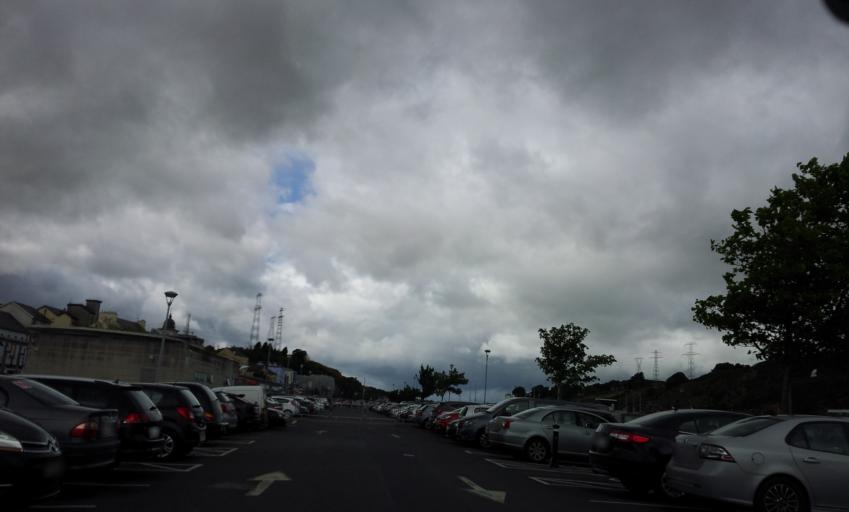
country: IE
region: Munster
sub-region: Waterford
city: Waterford
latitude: 52.2631
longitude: -7.1144
